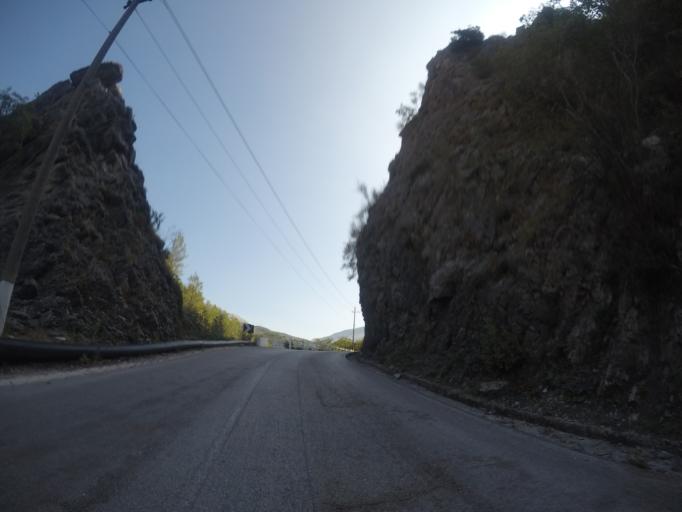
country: AL
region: Vlore
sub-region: Rrethi i Delvines
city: Mesopotam
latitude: 39.9191
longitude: 20.1431
